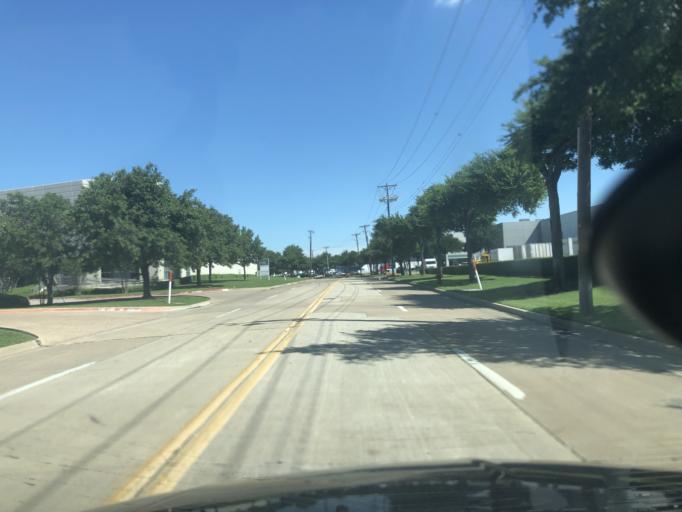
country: US
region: Texas
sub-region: Tarrant County
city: Euless
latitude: 32.7959
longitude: -97.0398
